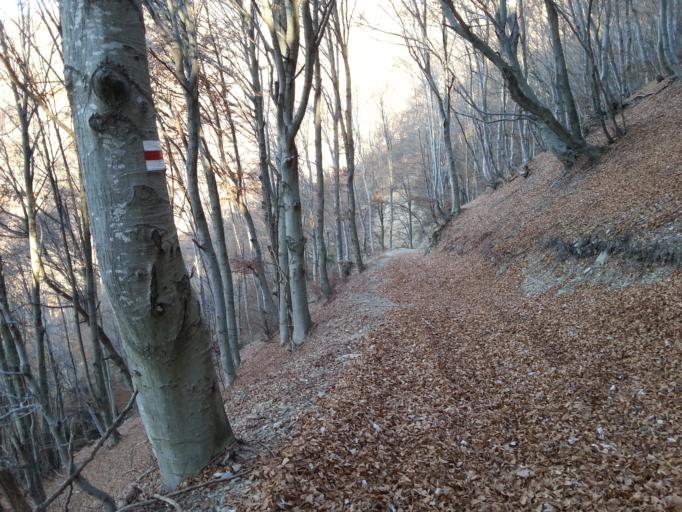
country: CH
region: Ticino
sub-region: Lugano District
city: Cadro
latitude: 46.0247
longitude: 9.0052
